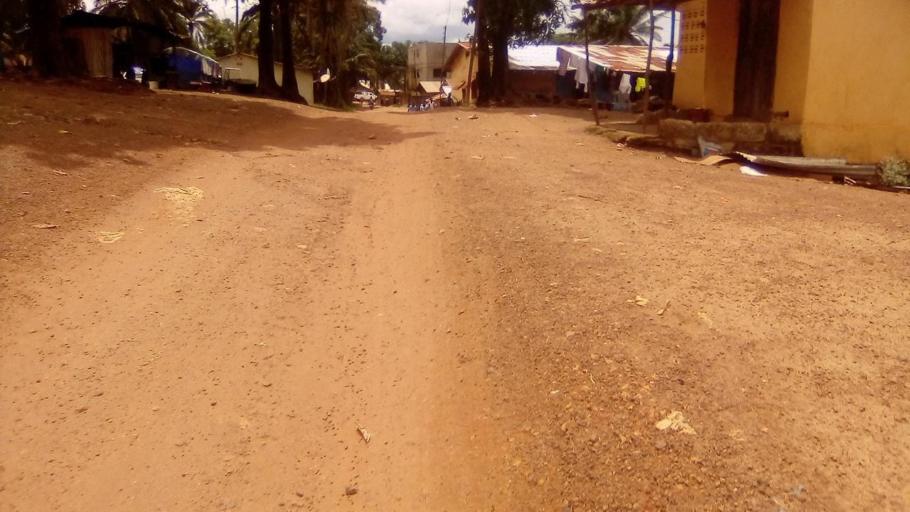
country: SL
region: Southern Province
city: Bo
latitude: 7.9427
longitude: -11.7324
